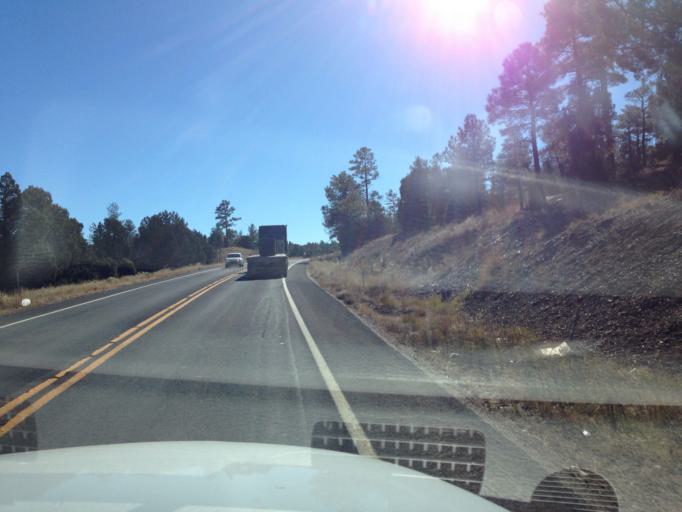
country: US
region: Arizona
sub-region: Navajo County
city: Linden
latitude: 34.2787
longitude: -110.0971
